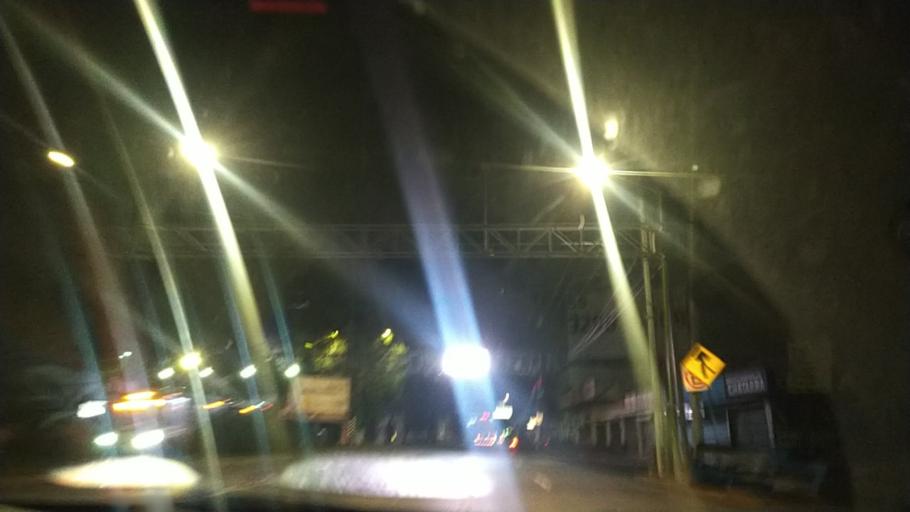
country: MX
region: Mexico
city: Ecatepec
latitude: 19.6128
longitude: -99.0601
